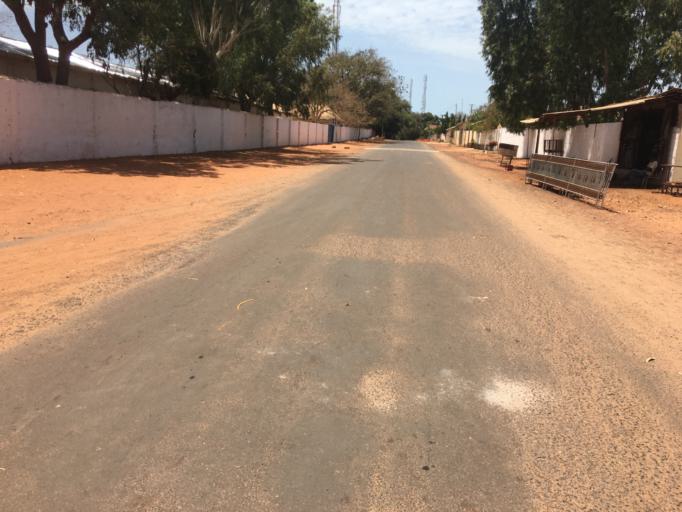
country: GM
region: Banjul
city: Bakau
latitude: 13.4720
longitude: -16.6843
